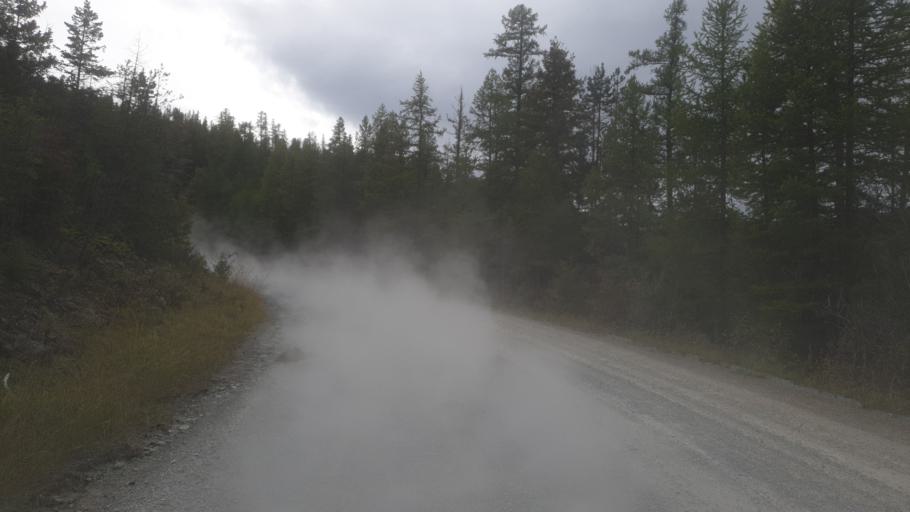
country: US
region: Montana
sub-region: Flathead County
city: Lakeside
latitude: 47.9935
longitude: -114.3237
